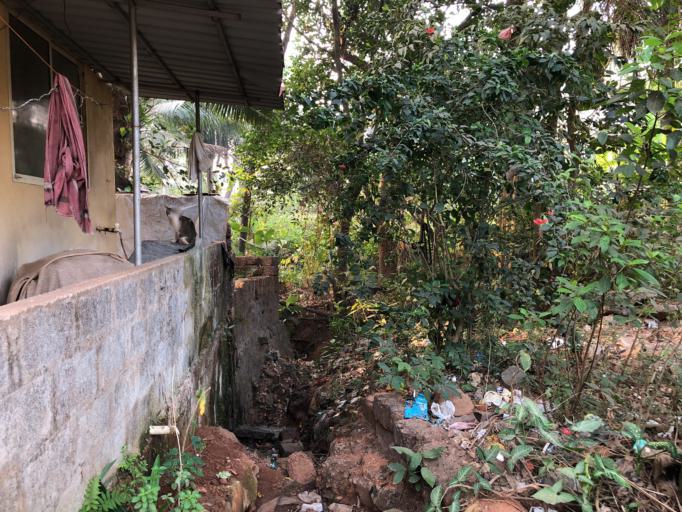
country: IN
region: Karnataka
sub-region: Dakshina Kannada
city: Mangalore
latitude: 12.8707
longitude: 74.8650
